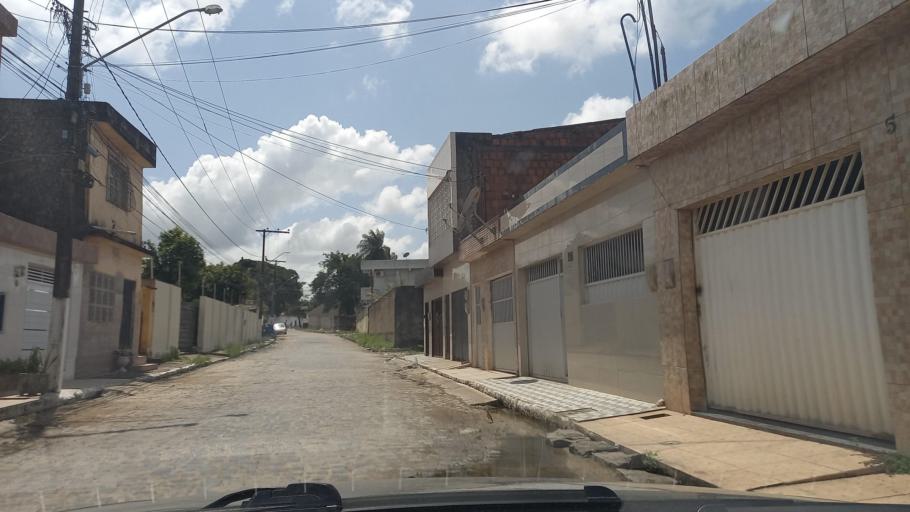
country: BR
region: Pernambuco
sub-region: Goiana
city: Goiana
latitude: -7.5659
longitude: -34.9975
